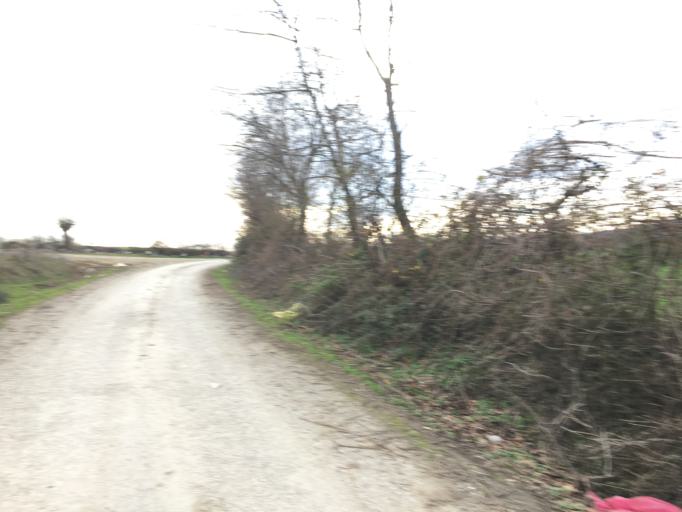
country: TR
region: Samsun
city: Alacam
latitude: 41.6002
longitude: 35.6103
